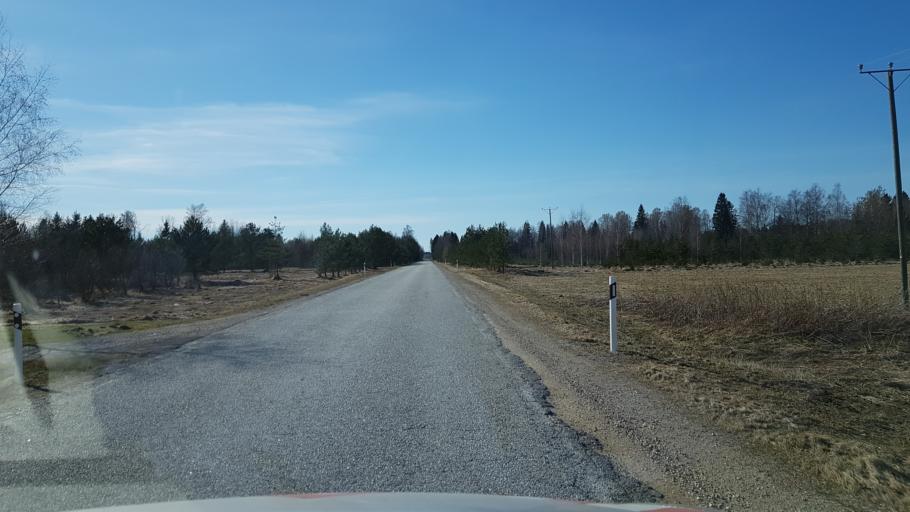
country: EE
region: Ida-Virumaa
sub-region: Kivioli linn
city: Kivioli
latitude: 59.2307
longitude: 26.7710
